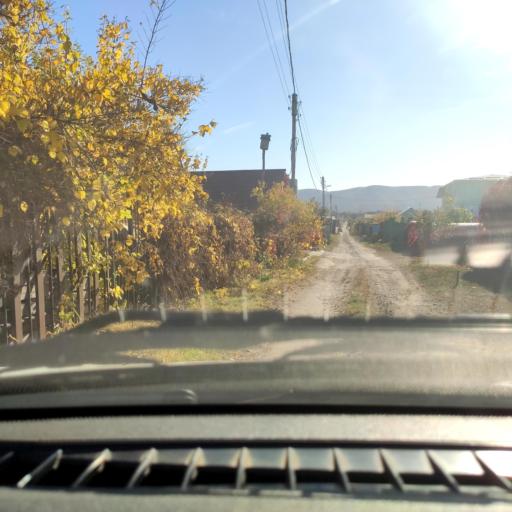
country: RU
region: Samara
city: Zhigulevsk
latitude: 53.4694
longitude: 49.5866
